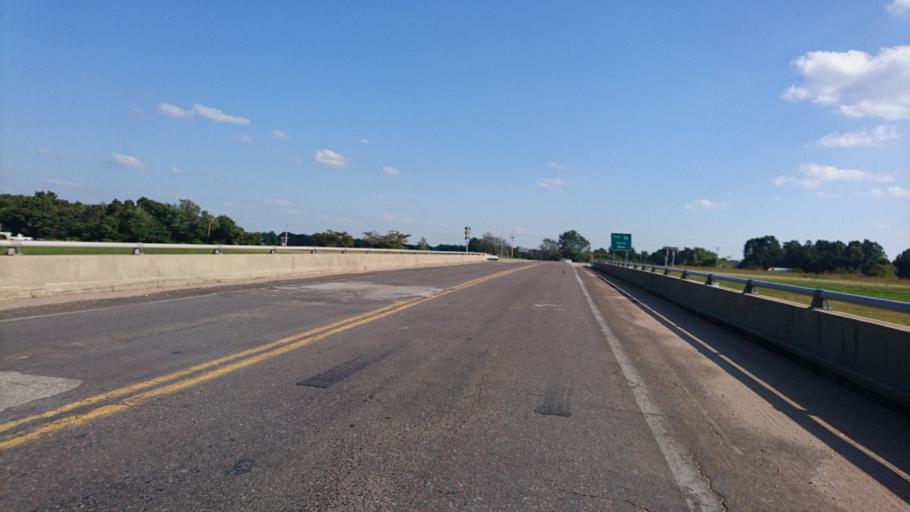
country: US
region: Missouri
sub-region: Laclede County
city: Lebanon
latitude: 37.5998
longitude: -92.7155
